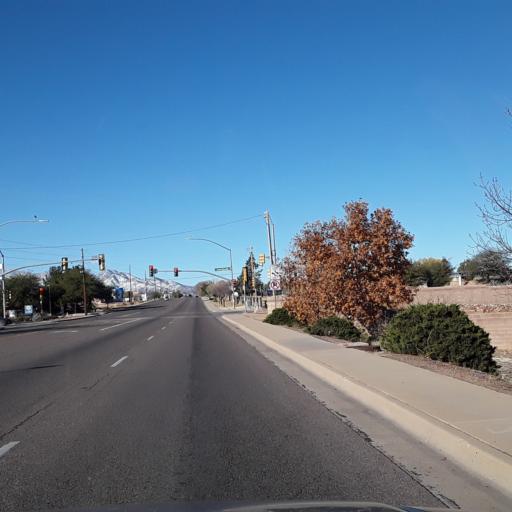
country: US
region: Arizona
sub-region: Cochise County
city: Sierra Vista
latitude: 31.5547
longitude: -110.2609
